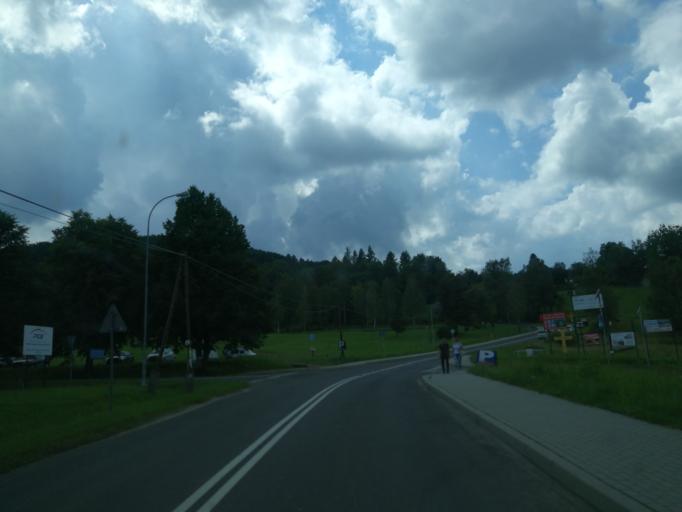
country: PL
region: Subcarpathian Voivodeship
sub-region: Powiat leski
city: Polanczyk
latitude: 49.4002
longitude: 22.4547
